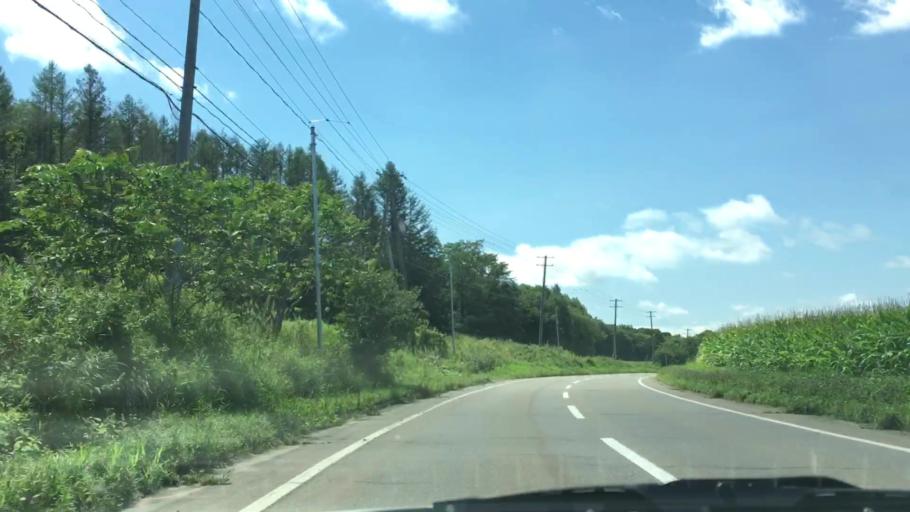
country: JP
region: Hokkaido
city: Kitami
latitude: 43.3241
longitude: 143.7311
